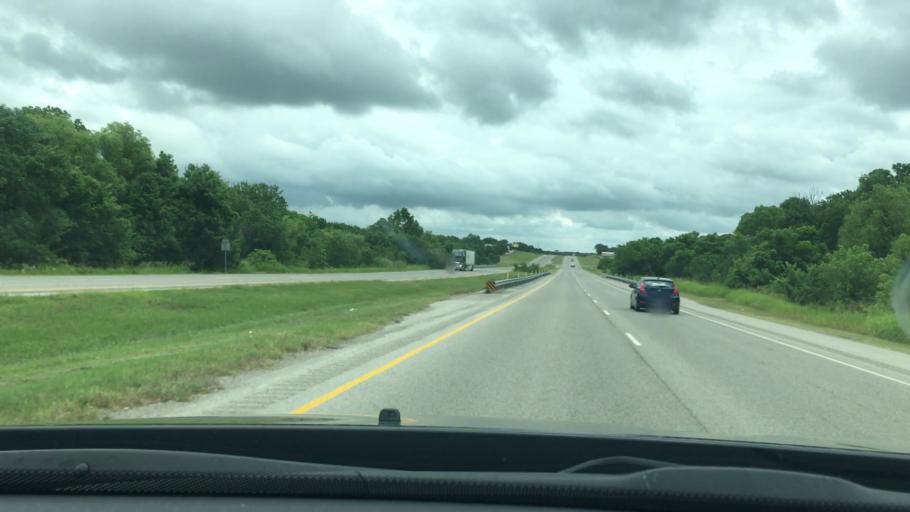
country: US
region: Oklahoma
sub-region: Carter County
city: Ardmore
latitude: 34.1351
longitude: -97.1055
